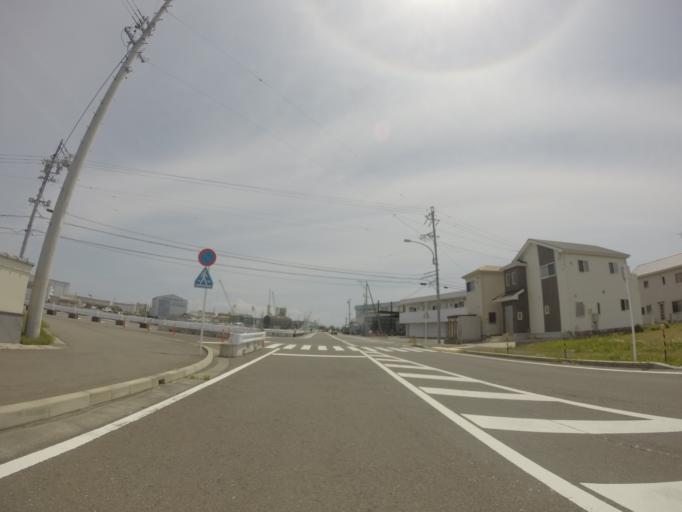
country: JP
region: Shizuoka
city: Yaizu
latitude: 34.8486
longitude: 138.3234
